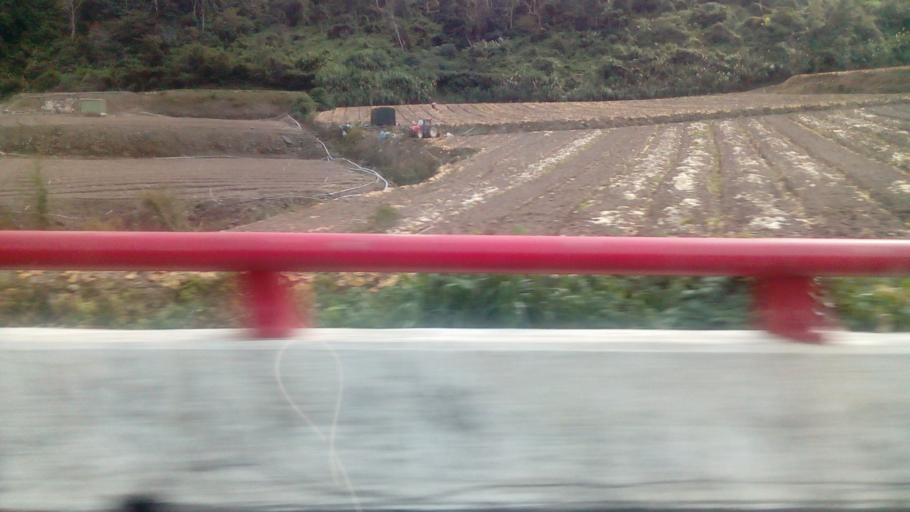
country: TW
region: Taiwan
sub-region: Yilan
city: Yilan
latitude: 24.5538
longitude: 121.4737
